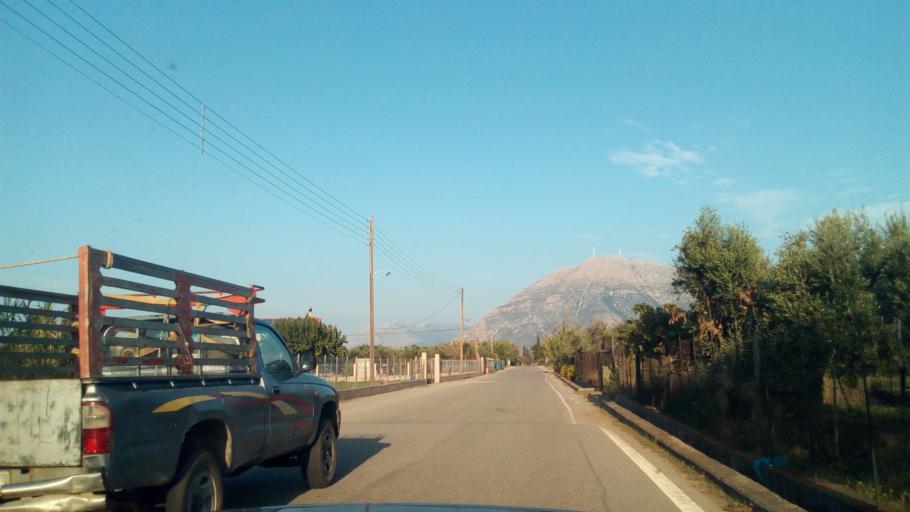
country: GR
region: West Greece
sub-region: Nomos Aitolias kai Akarnanias
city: Antirrio
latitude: 38.3342
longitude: 21.7558
